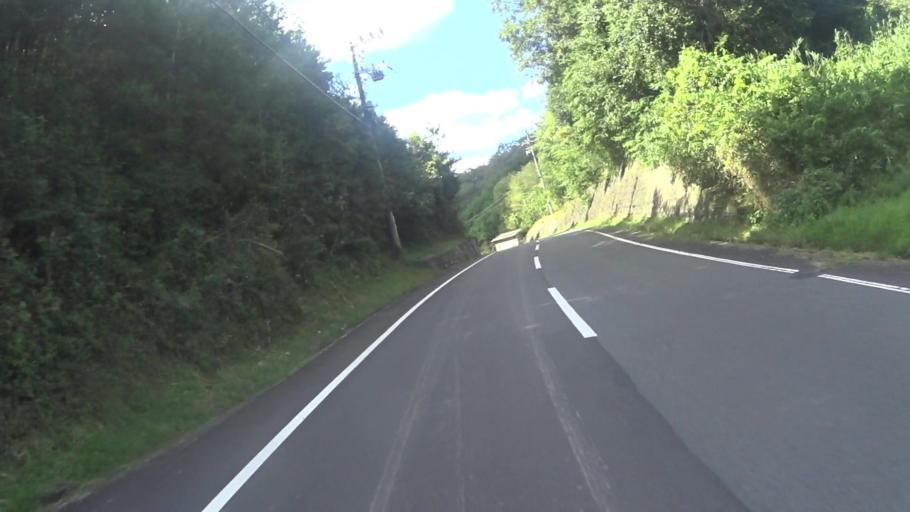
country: JP
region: Mie
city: Ueno-ebisumachi
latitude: 34.7268
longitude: 136.0228
